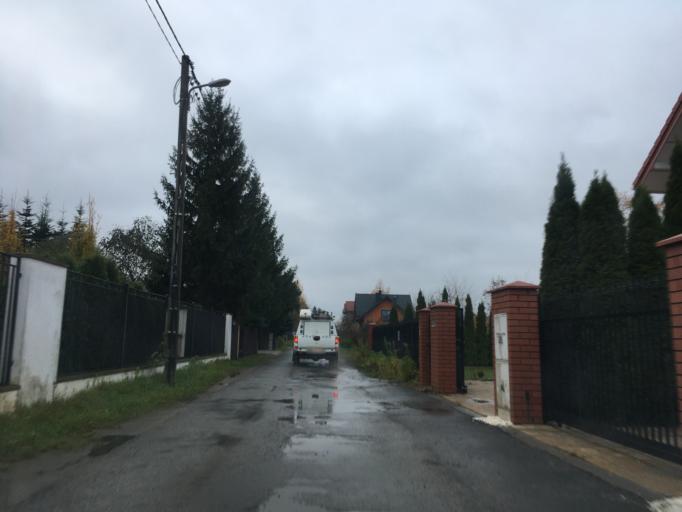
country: PL
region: Masovian Voivodeship
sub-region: Powiat pruszkowski
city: Brwinow
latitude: 52.1406
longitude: 20.7375
